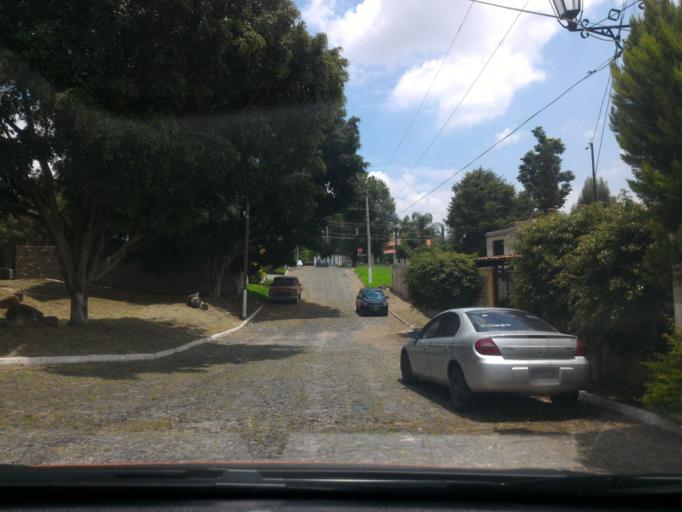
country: MX
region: Jalisco
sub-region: Tlajomulco de Zuniga
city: Santa Cruz de las Flores
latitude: 20.5007
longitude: -103.4978
